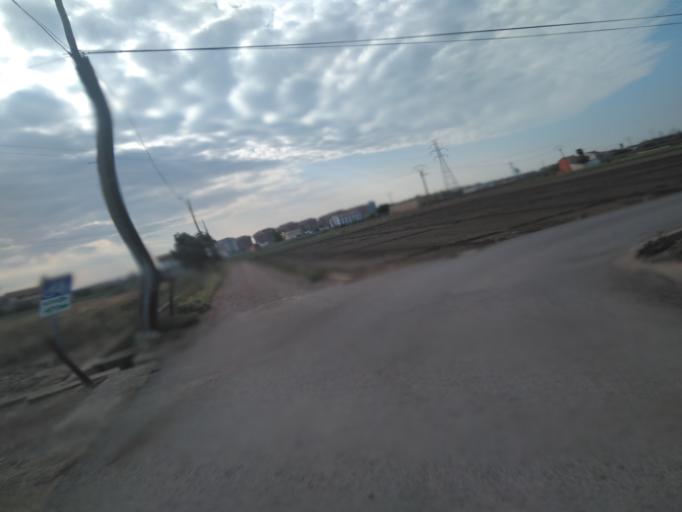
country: ES
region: Valencia
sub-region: Provincia de Valencia
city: Alboraya
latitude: 39.4936
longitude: -0.3396
